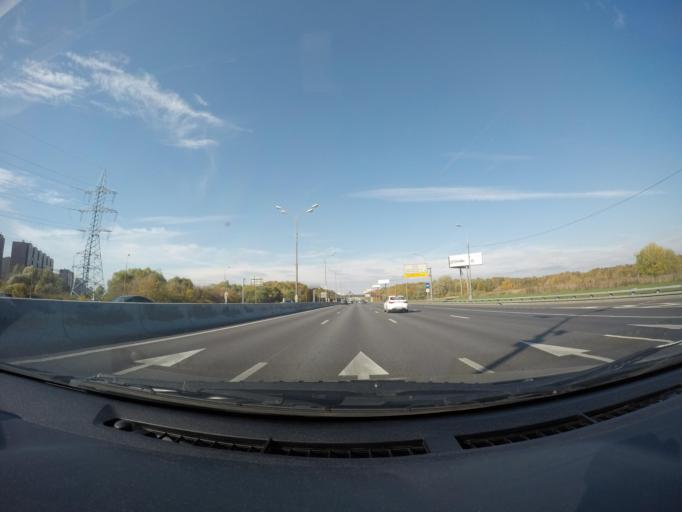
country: RU
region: Moscow
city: Gol'yanovo
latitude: 55.8304
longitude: 37.8273
